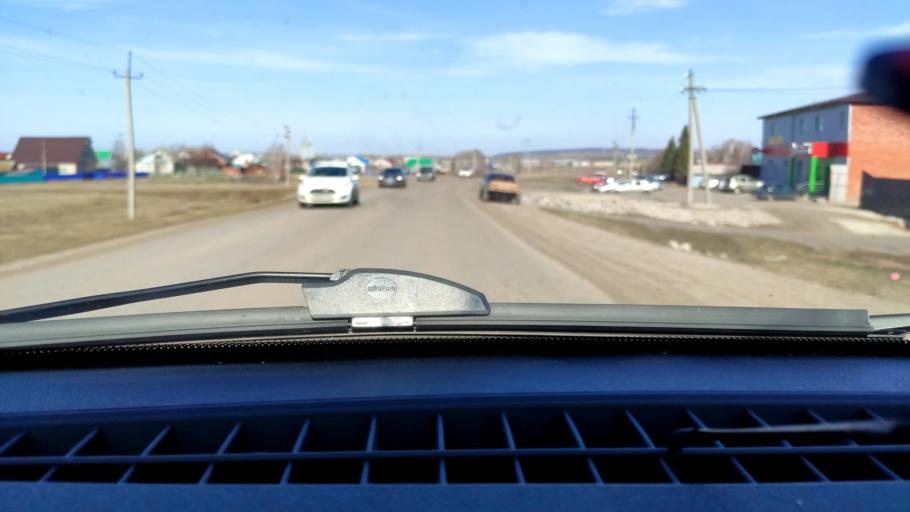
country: RU
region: Bashkortostan
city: Kabakovo
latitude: 54.5337
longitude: 56.1467
